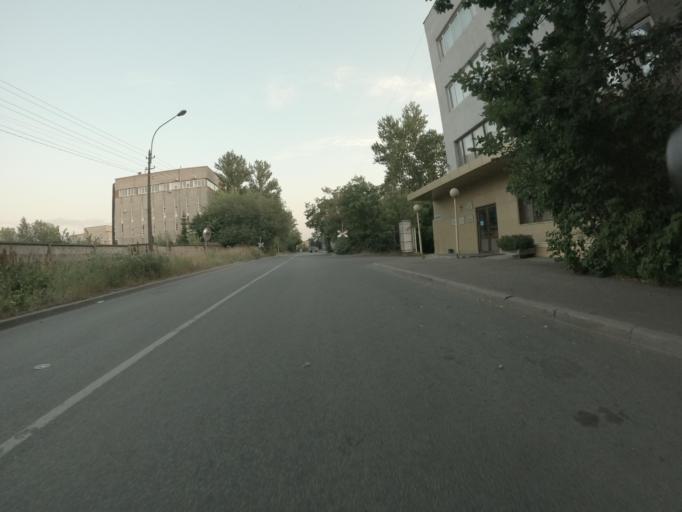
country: RU
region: St.-Petersburg
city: Kupchino
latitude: 59.8911
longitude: 30.3372
